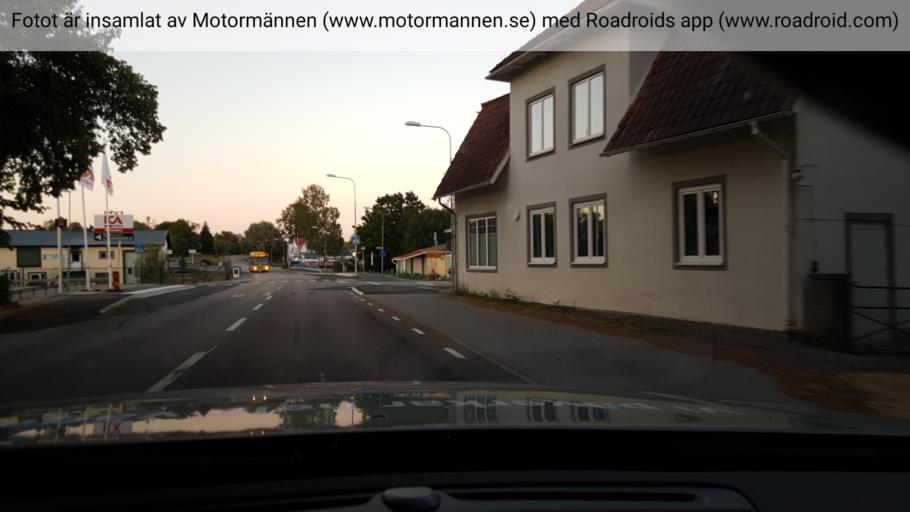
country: SE
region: Uppsala
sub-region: Heby Kommun
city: OEstervala
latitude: 60.1049
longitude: 17.1981
